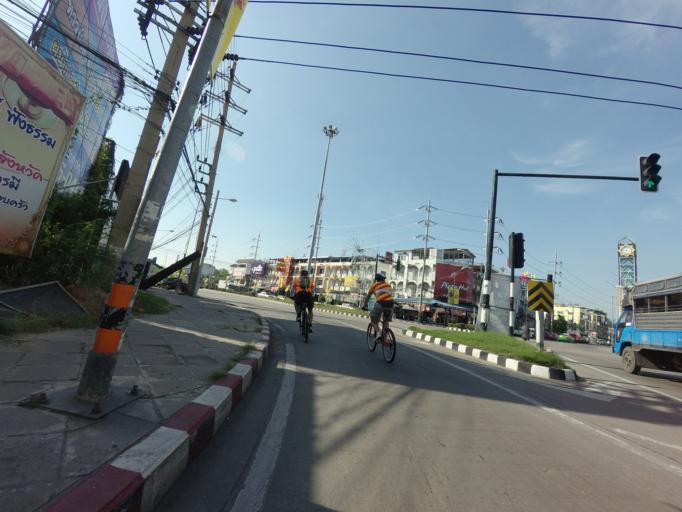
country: TH
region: Samut Prakan
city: Phra Samut Chedi
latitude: 13.5945
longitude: 100.5799
